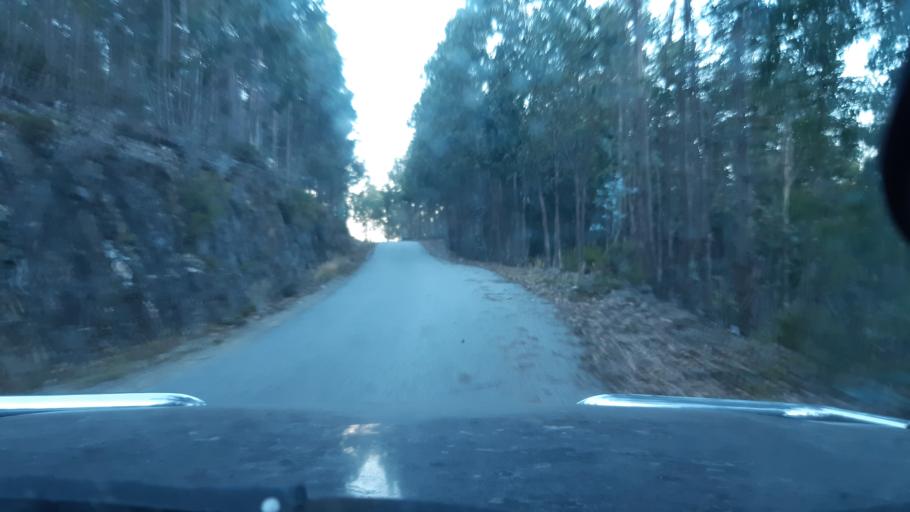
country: PT
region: Aveiro
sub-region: Agueda
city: Aguada de Cima
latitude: 40.5494
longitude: -8.2817
